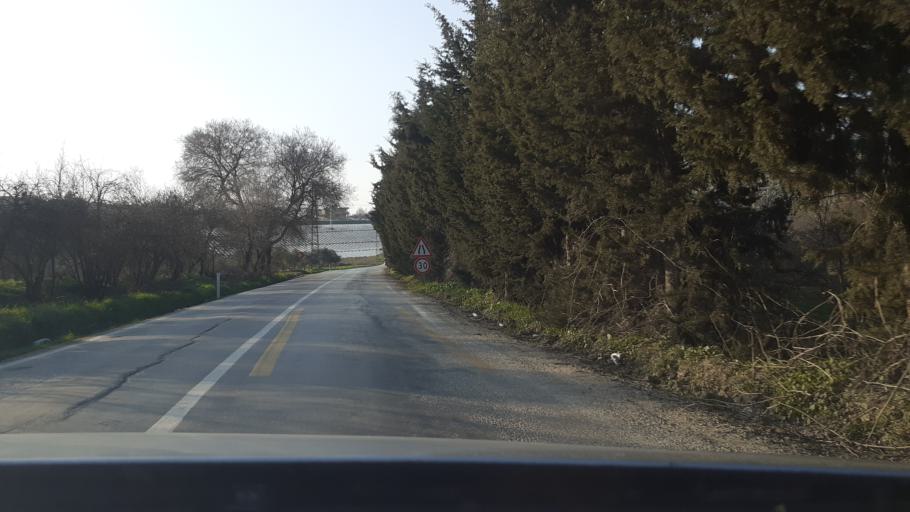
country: TR
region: Hatay
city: Fatikli
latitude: 36.1094
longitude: 36.2727
